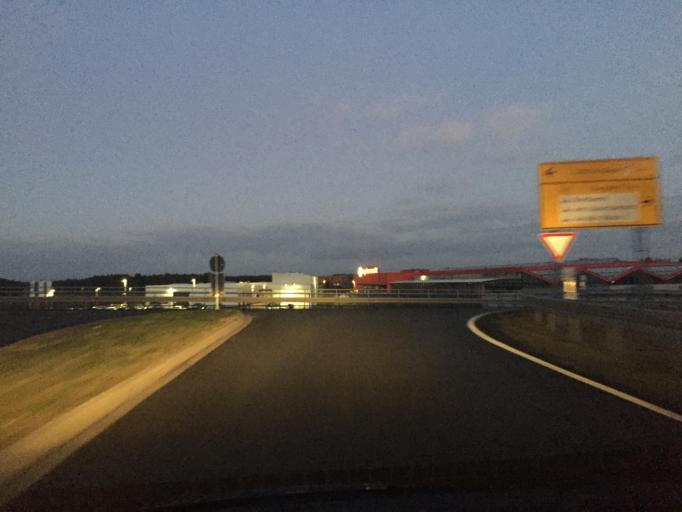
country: DE
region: Lower Saxony
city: Burgdorf
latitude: 52.4604
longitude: 9.9901
